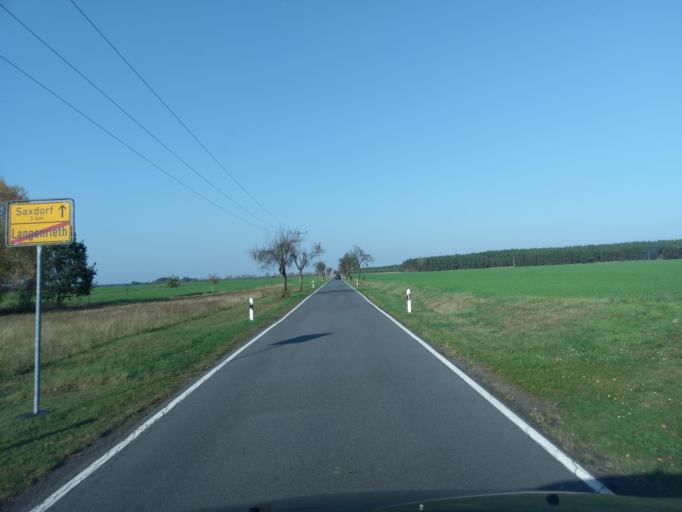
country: DE
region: Brandenburg
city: Muhlberg
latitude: 51.4772
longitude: 13.2715
